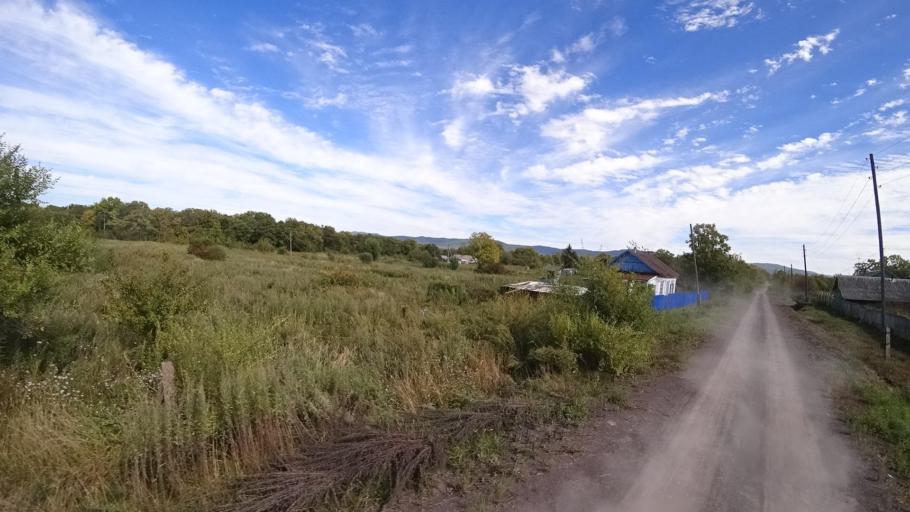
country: RU
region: Primorskiy
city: Yakovlevka
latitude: 44.4343
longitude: 133.5666
